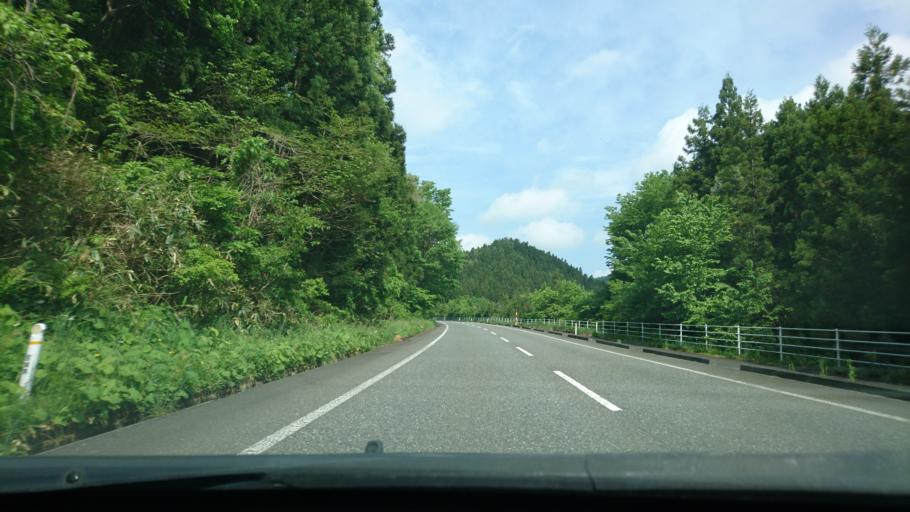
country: JP
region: Iwate
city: Ichinoseki
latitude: 38.8995
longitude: 140.9291
